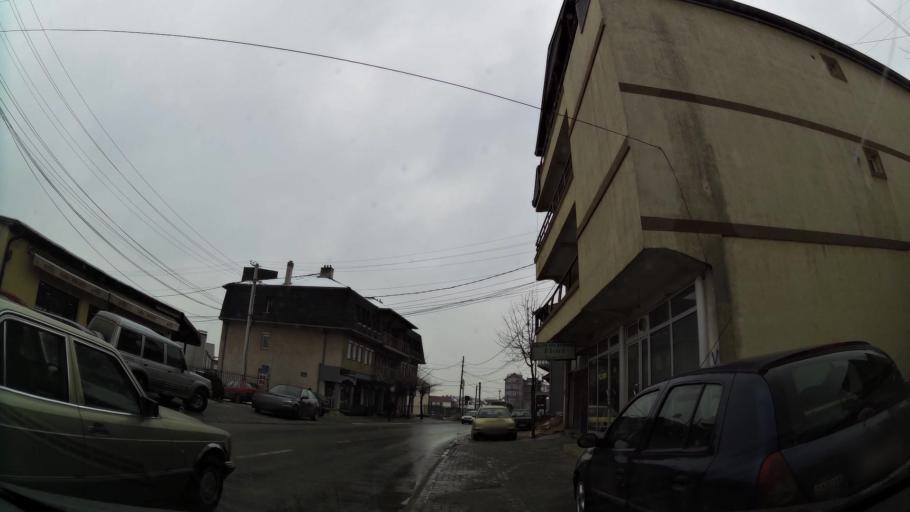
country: XK
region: Pristina
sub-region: Komuna e Prishtines
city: Pristina
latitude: 42.6767
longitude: 21.1706
